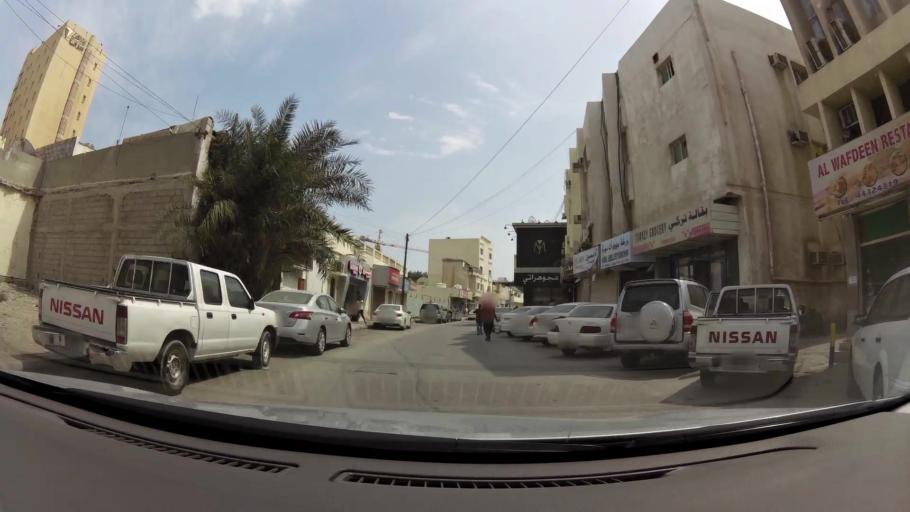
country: QA
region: Baladiyat ad Dawhah
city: Doha
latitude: 25.2857
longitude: 51.5380
